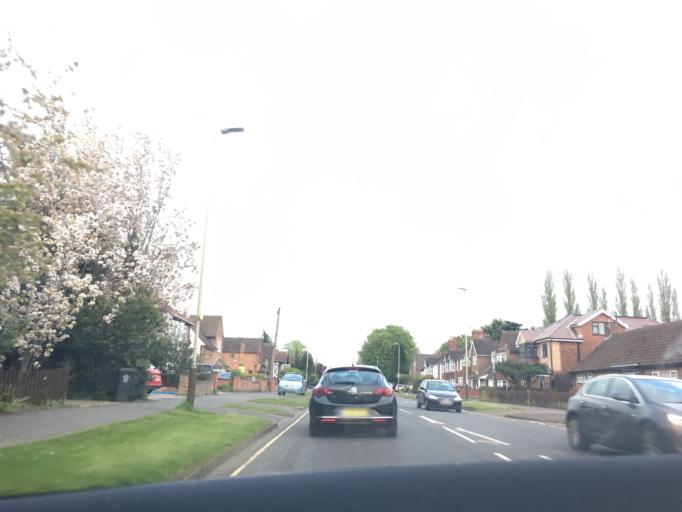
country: GB
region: England
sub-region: Leicestershire
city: Oadby
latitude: 52.6269
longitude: -1.0711
